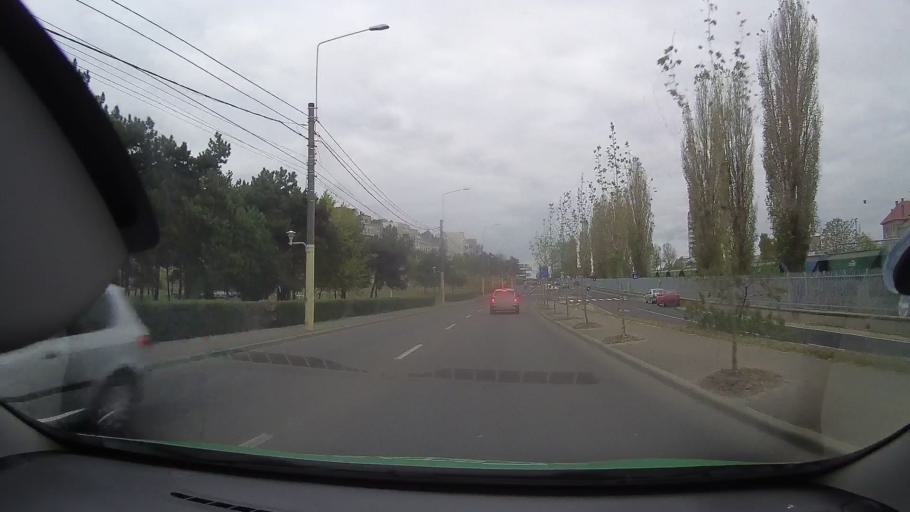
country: RO
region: Constanta
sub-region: Municipiul Constanta
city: Constanta
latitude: 44.1728
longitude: 28.6576
